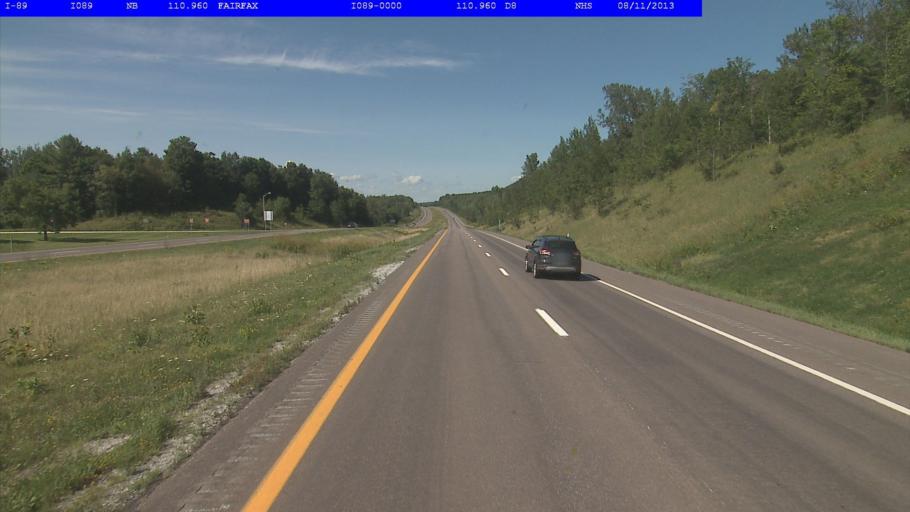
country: US
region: Vermont
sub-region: Franklin County
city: Saint Albans
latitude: 44.7550
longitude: -73.0772
